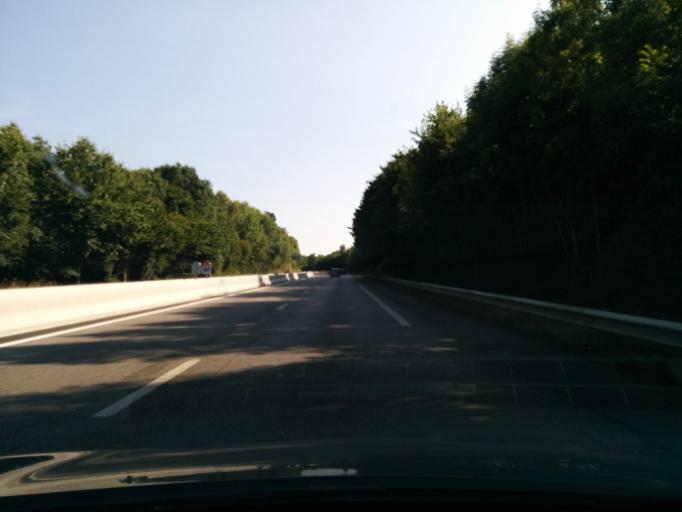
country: FR
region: Limousin
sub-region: Departement de la Haute-Vienne
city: Condat-sur-Vienne
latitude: 45.8040
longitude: 1.2969
